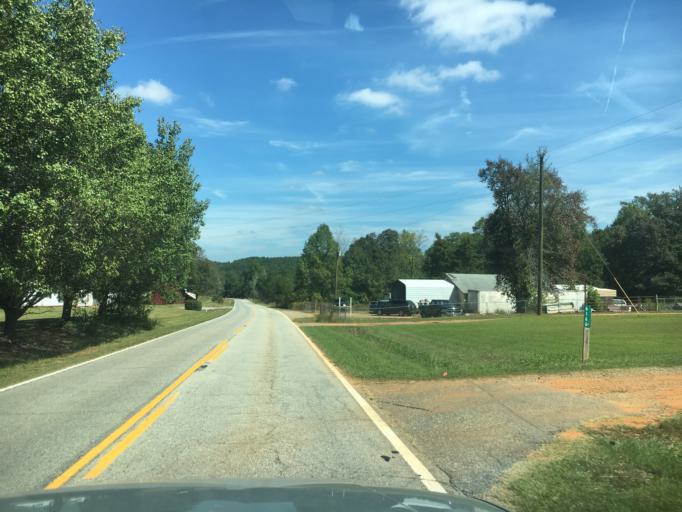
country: US
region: South Carolina
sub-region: Spartanburg County
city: Mayo
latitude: 35.1009
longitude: -81.9230
